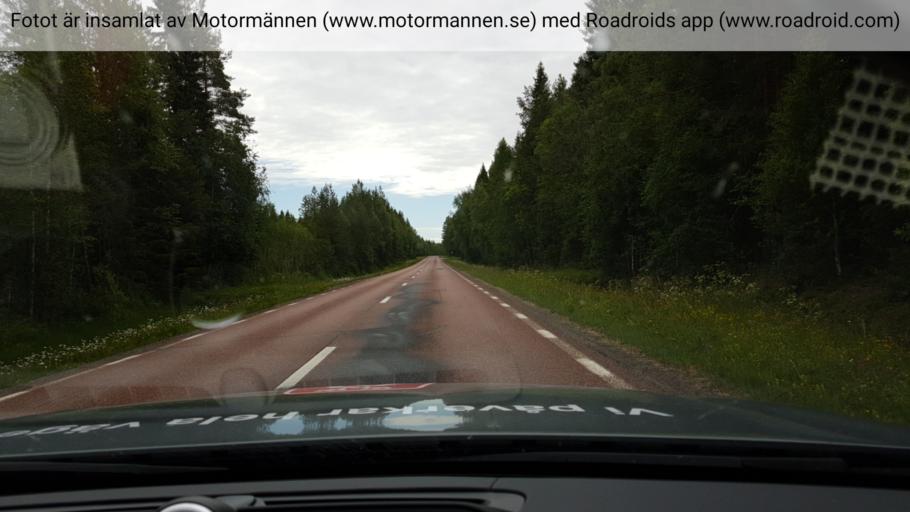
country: SE
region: Vaesterbotten
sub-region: Dorotea Kommun
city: Dorotea
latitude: 64.0865
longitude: 16.0861
